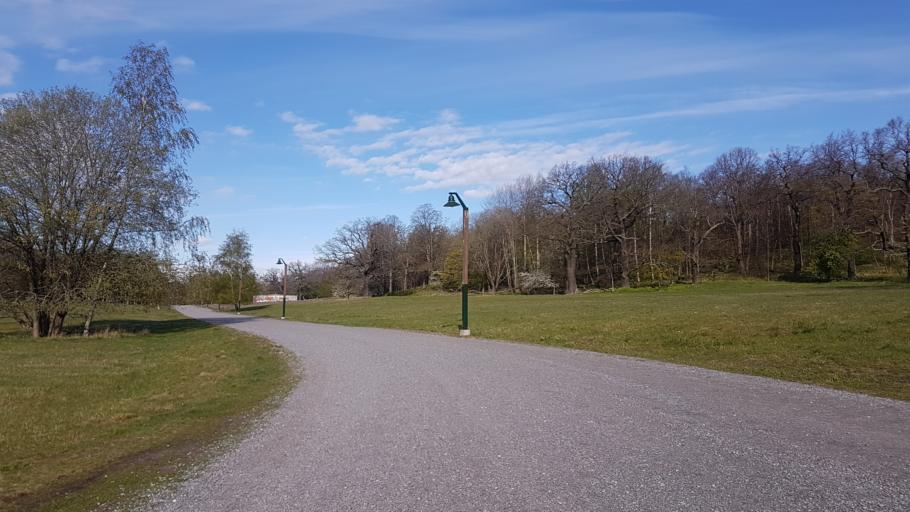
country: SE
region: Stockholm
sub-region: Stockholms Kommun
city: OEstermalm
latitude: 59.3620
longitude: 18.0956
